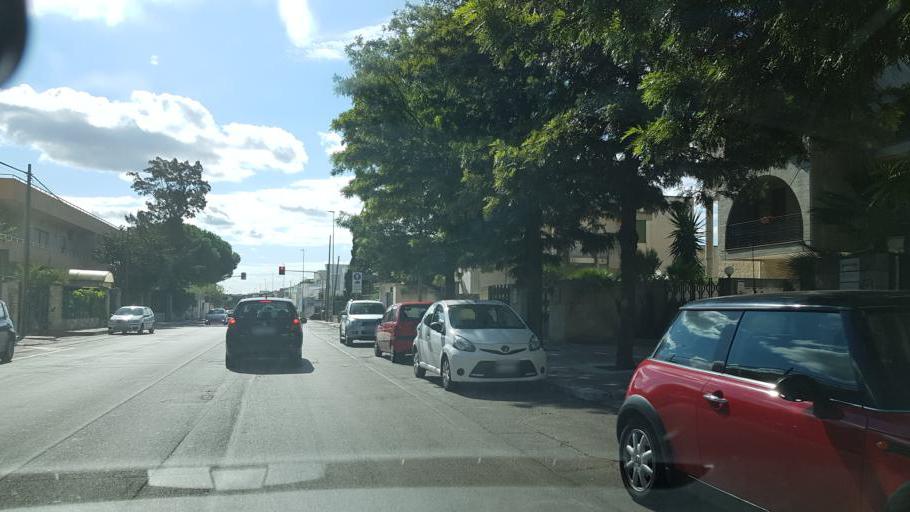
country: IT
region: Apulia
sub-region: Provincia di Lecce
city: Lecce
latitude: 40.3511
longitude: 18.1515
